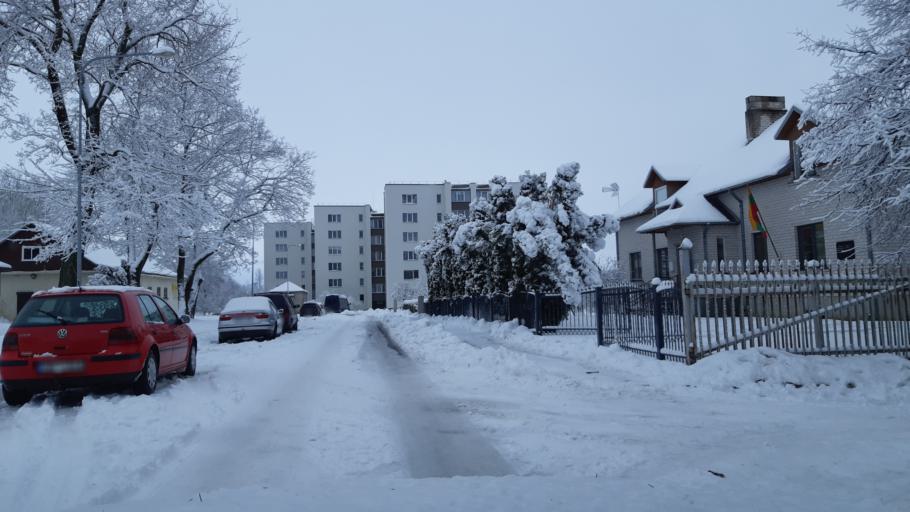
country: LT
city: Kybartai
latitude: 54.6378
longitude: 22.7566
